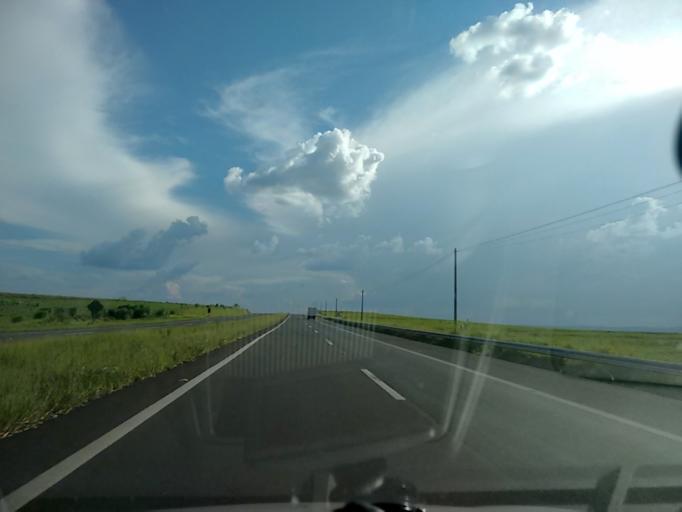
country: BR
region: Sao Paulo
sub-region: Duartina
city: Duartina
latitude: -22.2880
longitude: -49.4926
